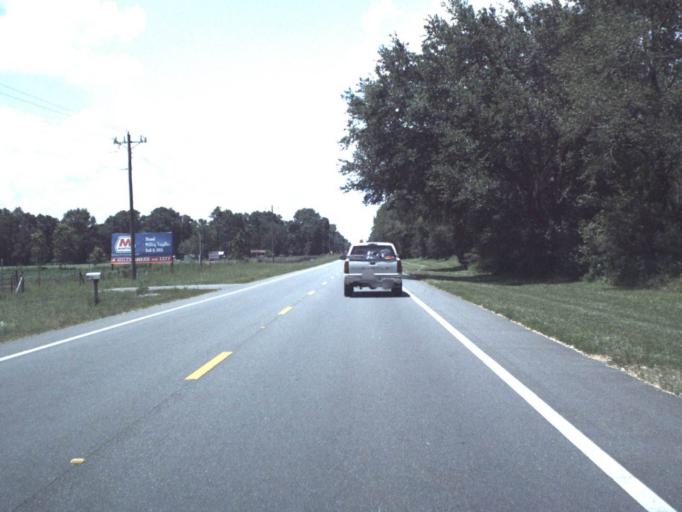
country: US
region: Florida
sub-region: Dixie County
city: Cross City
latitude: 29.7307
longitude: -82.9846
